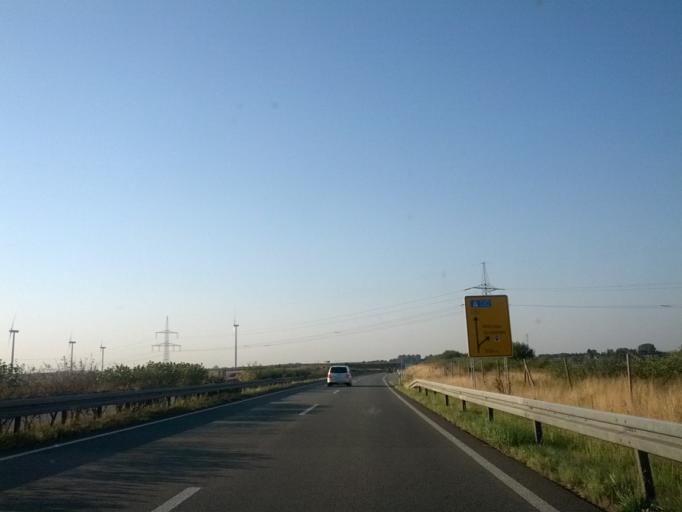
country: DE
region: Mecklenburg-Vorpommern
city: Brandshagen
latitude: 54.1734
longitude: 13.1749
